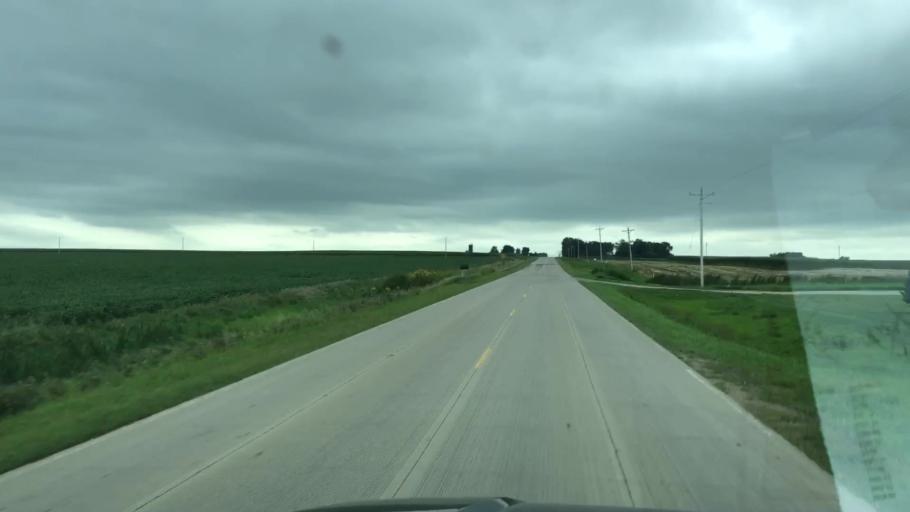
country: US
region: Iowa
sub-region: Sioux County
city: Alton
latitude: 43.1024
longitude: -95.9785
